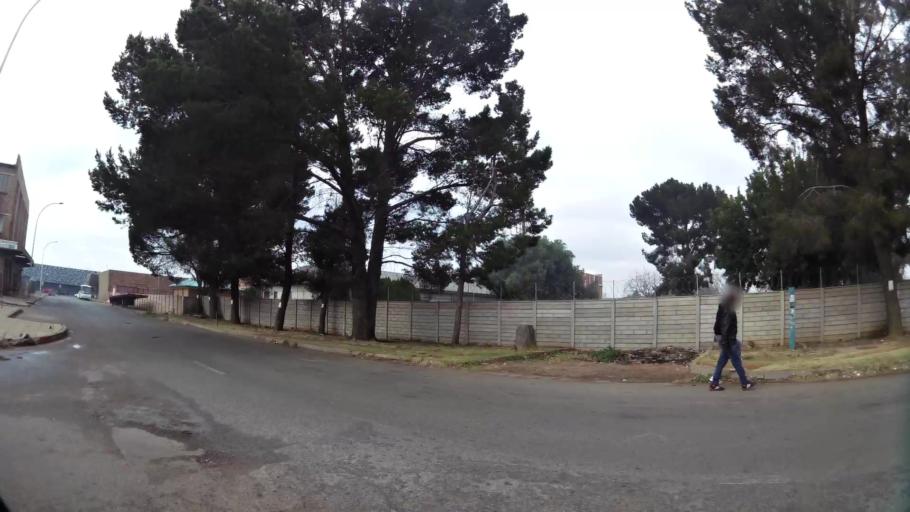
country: ZA
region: Gauteng
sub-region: Sedibeng District Municipality
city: Vanderbijlpark
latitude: -26.7014
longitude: 27.8361
